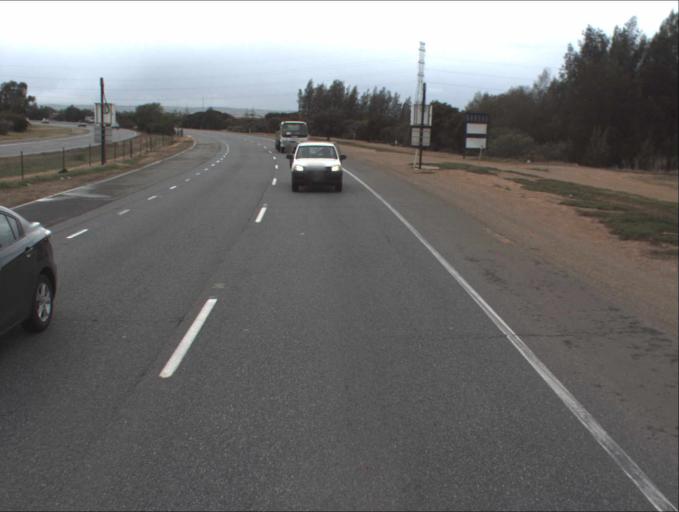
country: AU
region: South Australia
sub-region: Port Adelaide Enfield
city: Enfield
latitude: -34.8328
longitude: 138.5806
